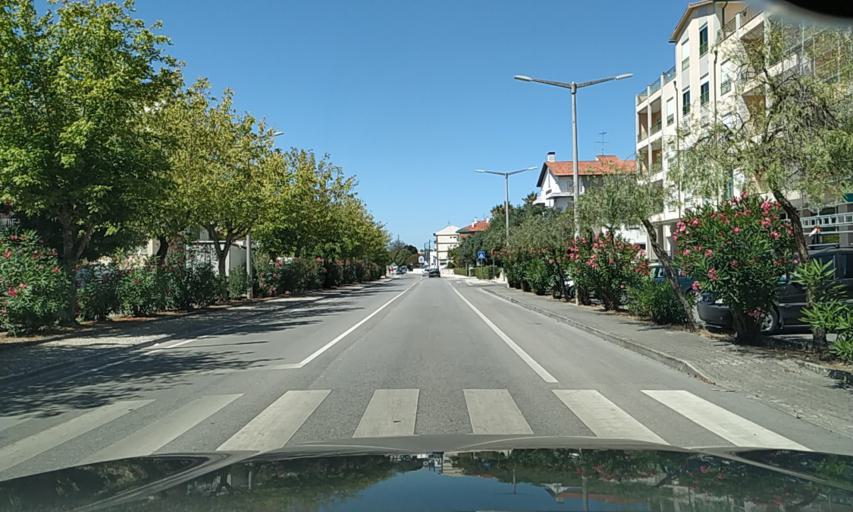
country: PT
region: Leiria
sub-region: Leiria
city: Leiria
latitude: 39.7578
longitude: -8.8197
